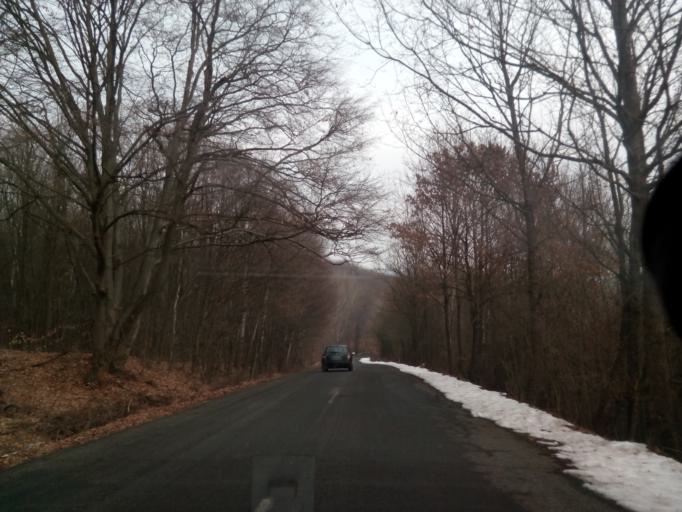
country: HU
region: Borsod-Abauj-Zemplen
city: Gonc
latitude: 48.4857
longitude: 21.3961
